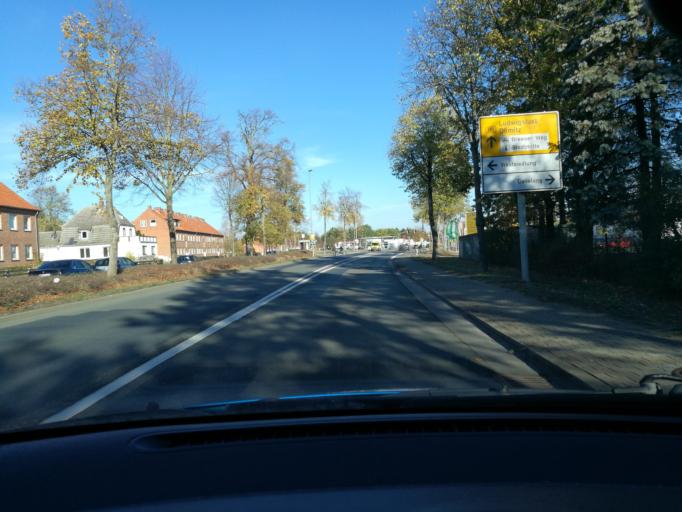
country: DE
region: Lower Saxony
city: Dannenberg
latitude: 53.0902
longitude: 11.0859
